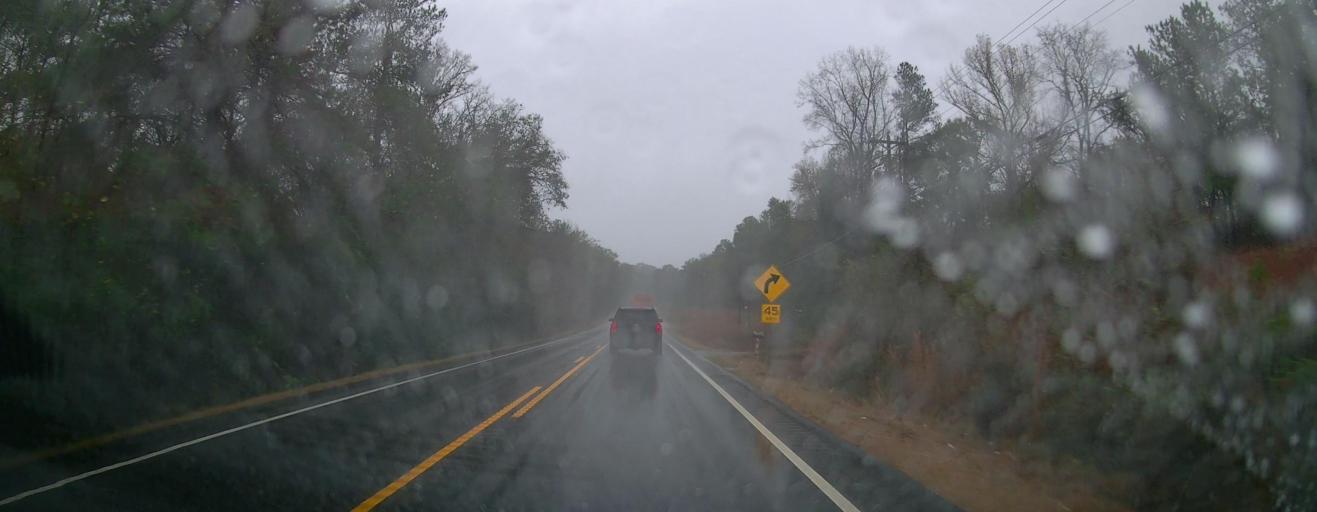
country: US
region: Georgia
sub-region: Putnam County
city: Eatonton
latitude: 33.2309
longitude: -83.4335
